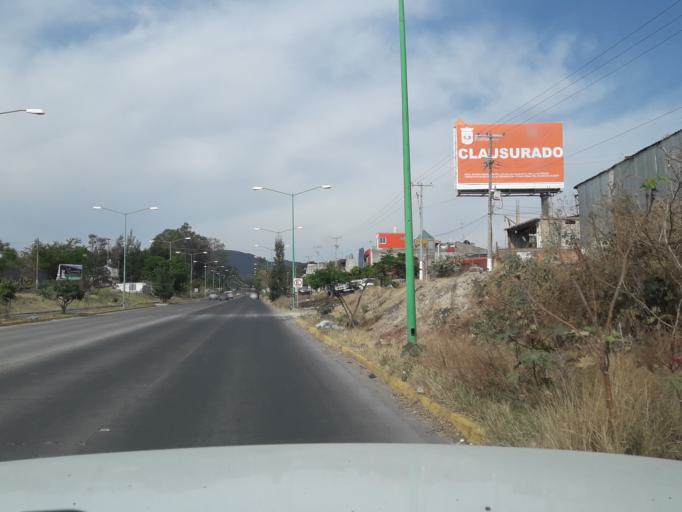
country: MX
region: Jalisco
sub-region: Tlajomulco de Zuniga
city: Palomar
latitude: 20.6217
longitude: -103.4737
